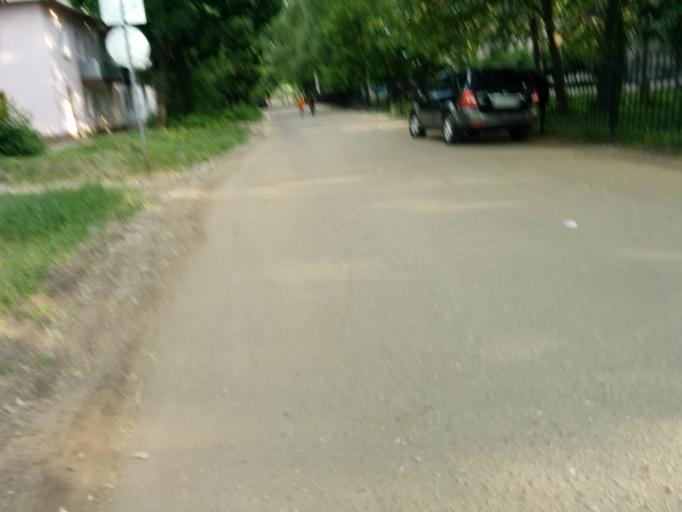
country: RU
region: Tambov
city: Tambov
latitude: 52.7479
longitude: 41.4410
